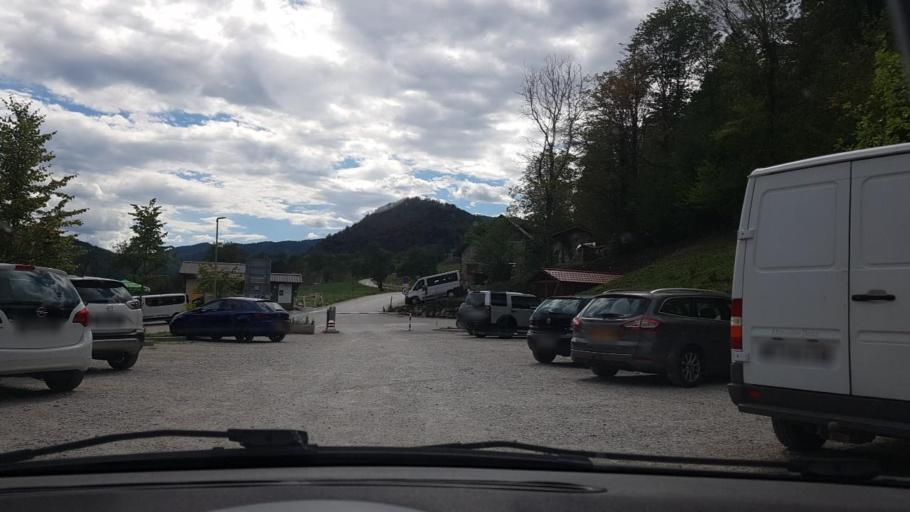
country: SI
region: Tolmin
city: Tolmin
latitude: 46.1978
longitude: 13.7395
